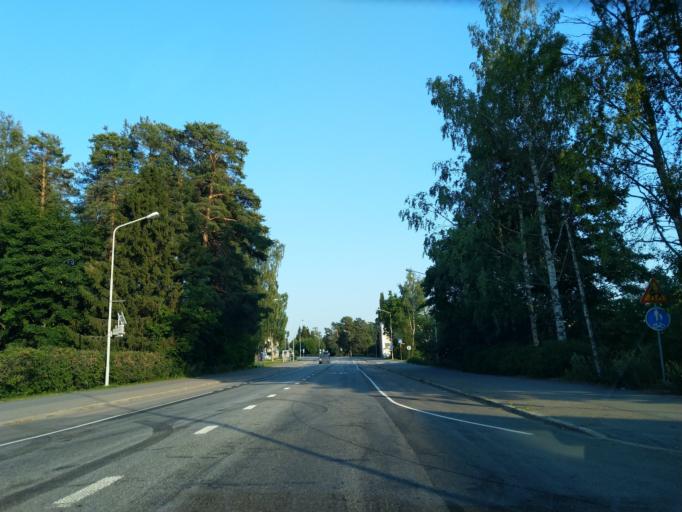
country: FI
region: Satakunta
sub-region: Pohjois-Satakunta
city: Kankaanpaeae
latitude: 61.8091
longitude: 22.3839
